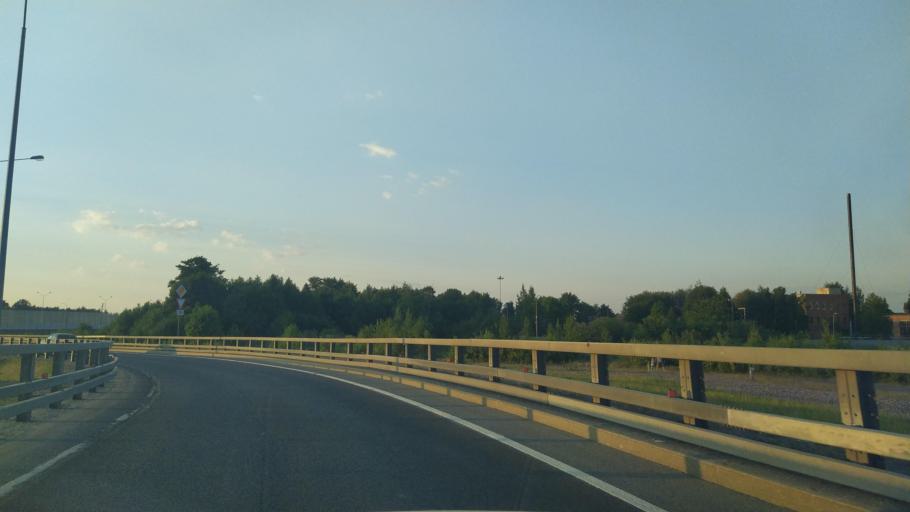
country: RU
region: St.-Petersburg
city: Kronshtadt
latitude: 60.0139
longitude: 29.7225
